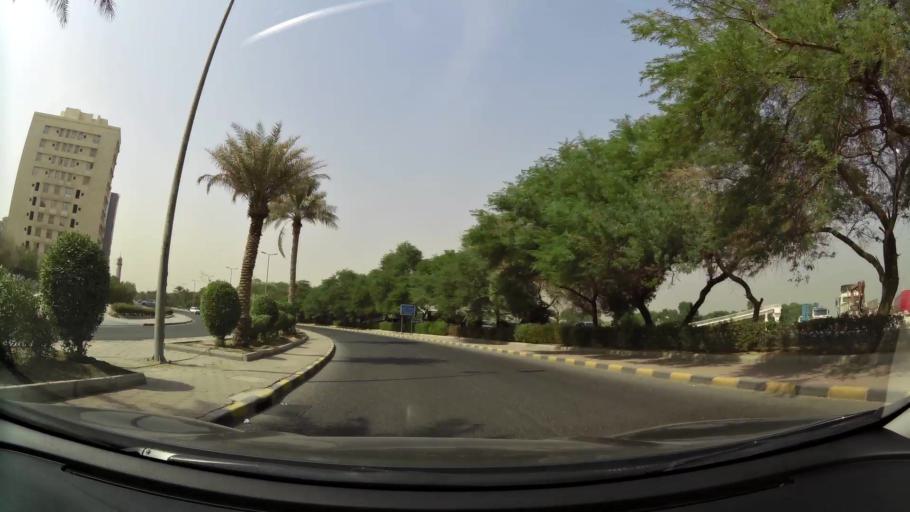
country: KW
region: Al Asimah
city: Ar Rabiyah
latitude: 29.3100
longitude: 47.9201
